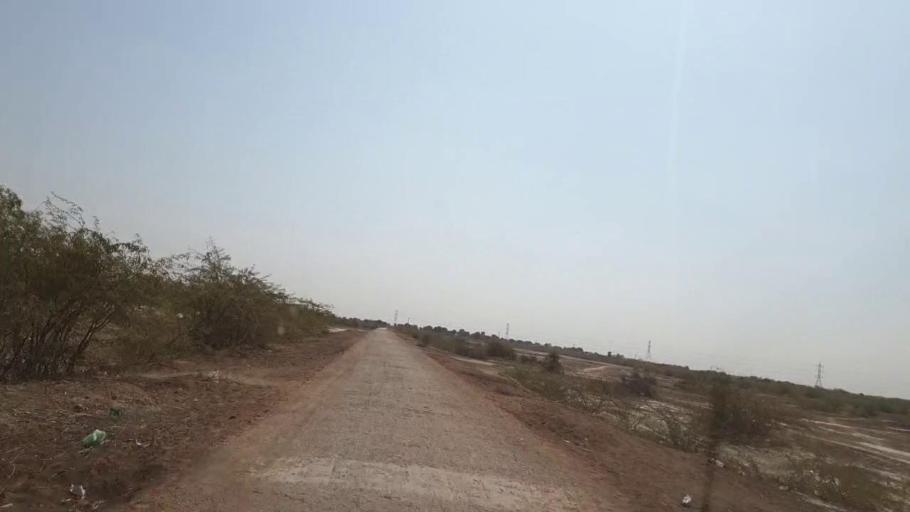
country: PK
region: Sindh
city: Nabisar
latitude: 25.0720
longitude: 69.5487
